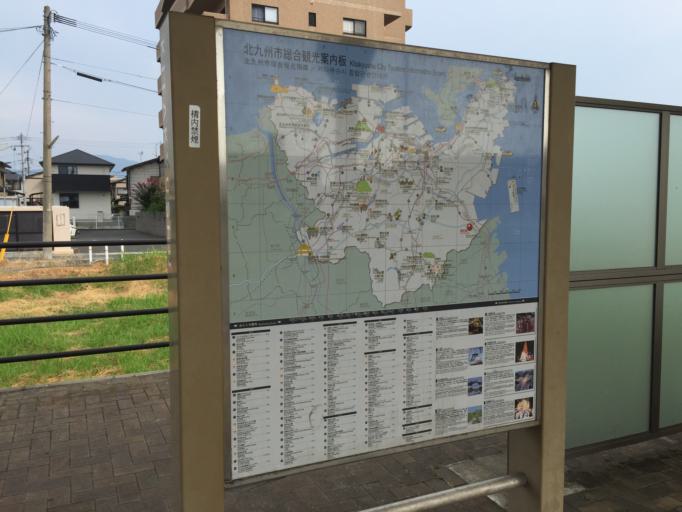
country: JP
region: Fukuoka
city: Kanda
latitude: 33.8077
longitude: 130.9555
